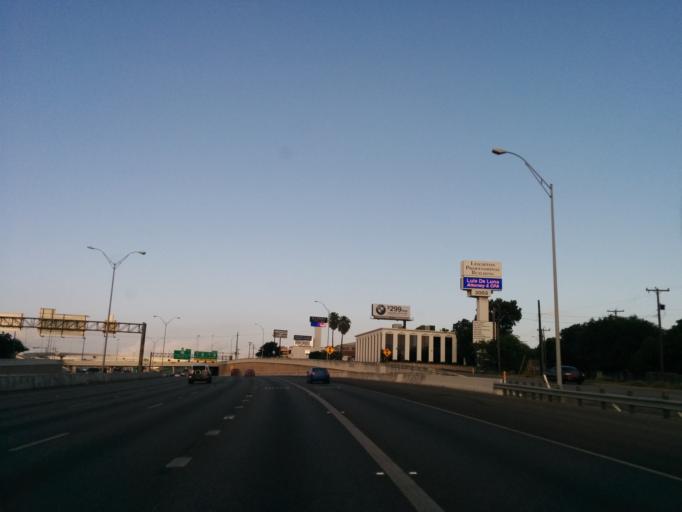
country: US
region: Texas
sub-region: Bexar County
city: Balcones Heights
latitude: 29.5093
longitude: -98.5418
